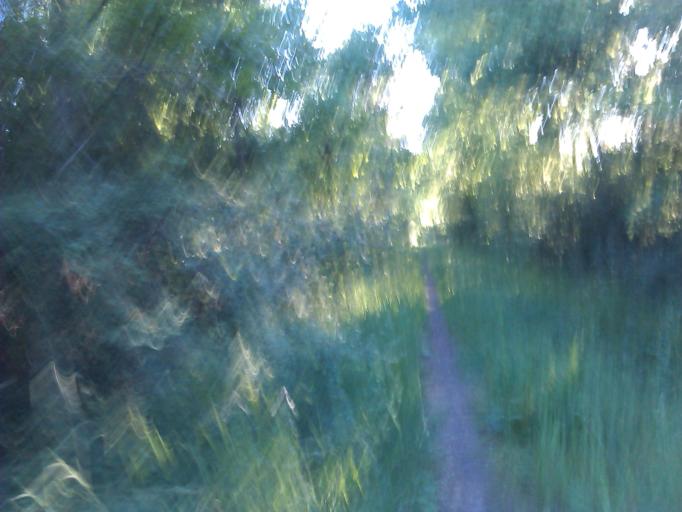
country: FR
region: Centre
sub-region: Departement de l'Indre
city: Le Blanc
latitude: 46.6003
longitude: 0.9877
